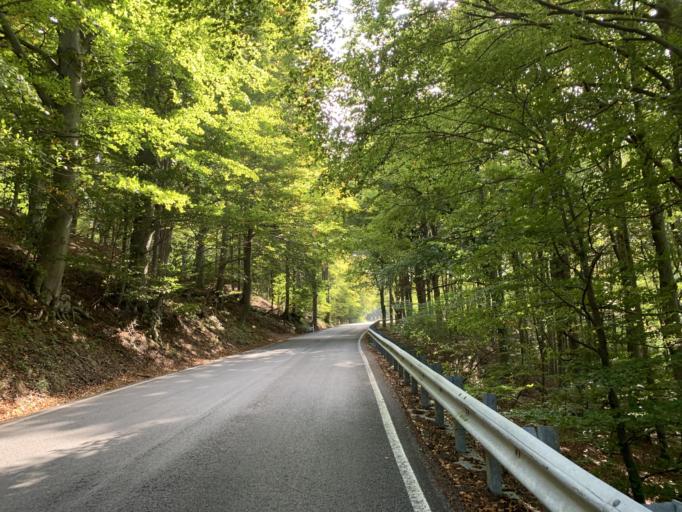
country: IT
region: Liguria
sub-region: Provincia di Savona
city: Osiglia
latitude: 44.2326
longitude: 8.1956
